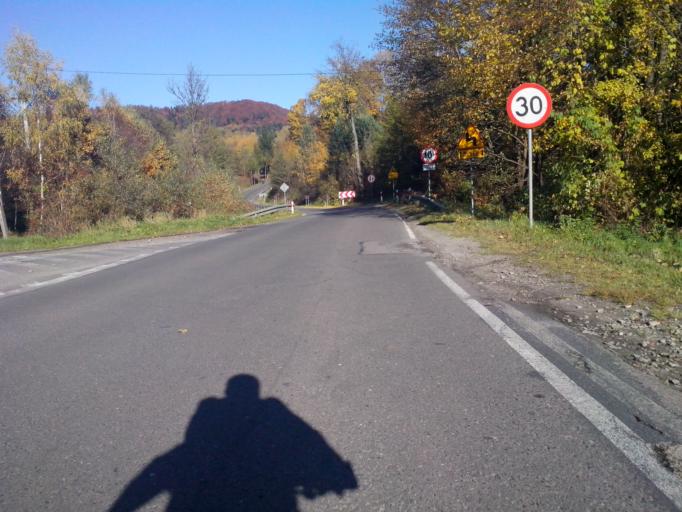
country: PL
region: Subcarpathian Voivodeship
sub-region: Powiat krosnienski
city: Korczyna
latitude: 49.7647
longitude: 21.7990
